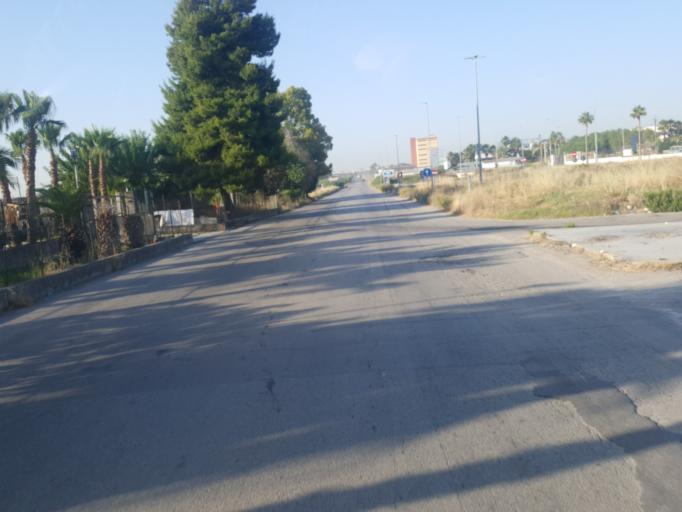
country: IT
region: Apulia
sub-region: Provincia di Foggia
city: Cerignola
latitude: 41.3059
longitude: 15.8986
